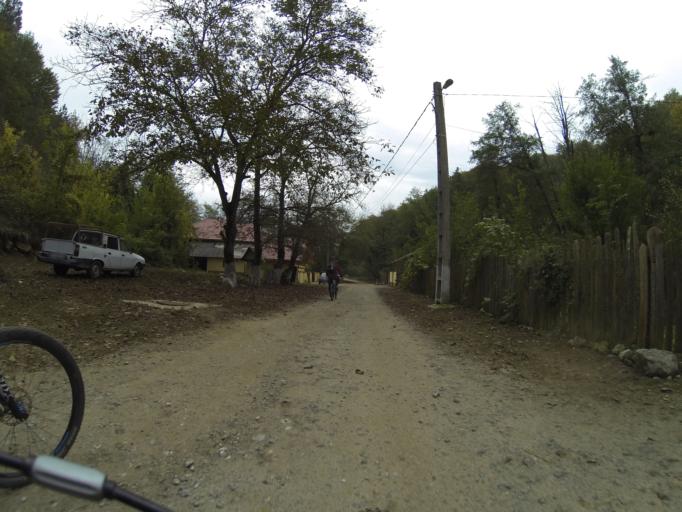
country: RO
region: Gorj
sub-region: Comuna Tismana
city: Pocruia
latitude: 45.0514
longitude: 22.9157
